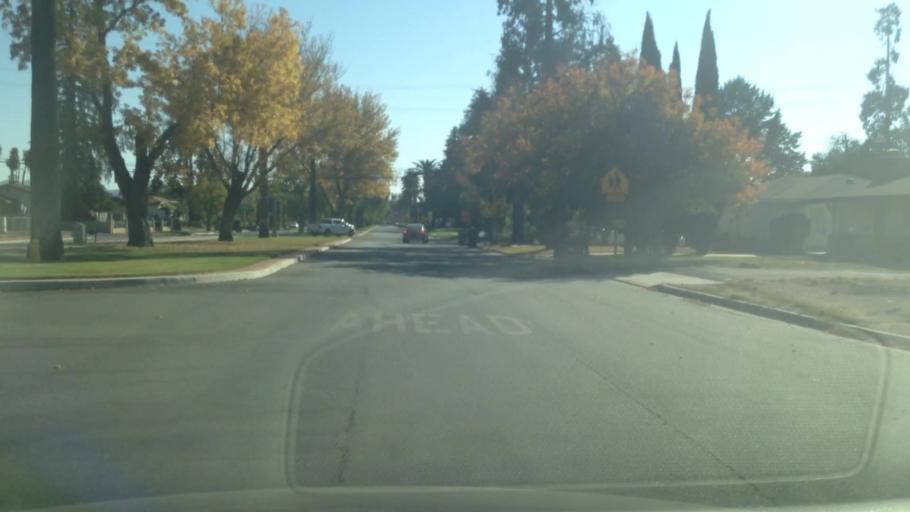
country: US
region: California
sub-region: Riverside County
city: Beaumont
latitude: 33.9333
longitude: -116.9718
